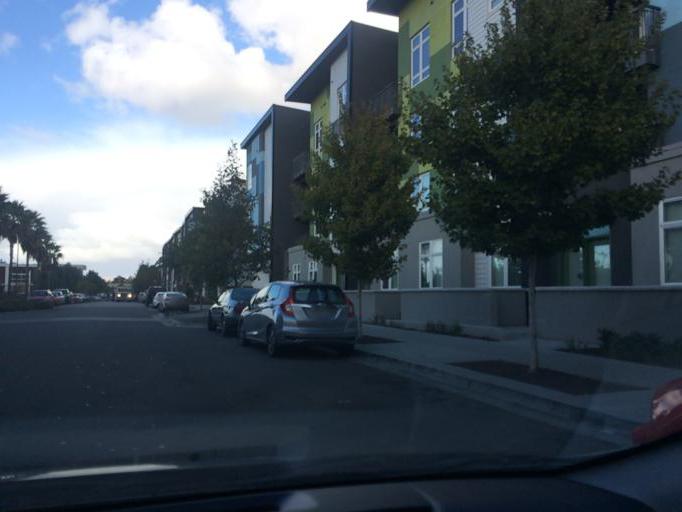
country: US
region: California
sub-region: Santa Clara County
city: Seven Trees
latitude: 37.2465
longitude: -121.8023
